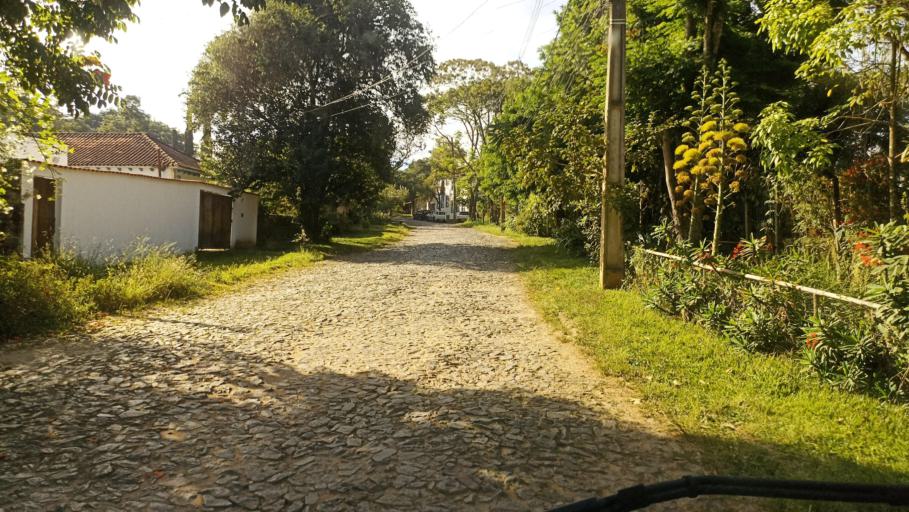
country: BR
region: Minas Gerais
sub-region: Tiradentes
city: Tiradentes
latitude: -21.1133
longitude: -44.1863
